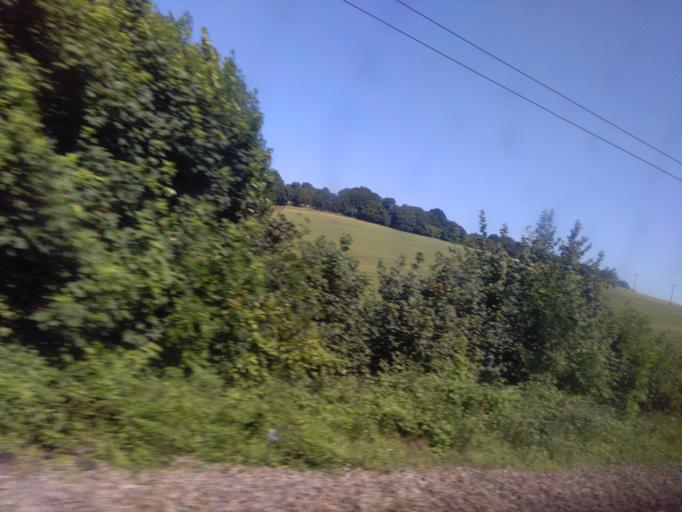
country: GB
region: England
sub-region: Hertfordshire
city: Harpenden
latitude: 51.8566
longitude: -0.3774
